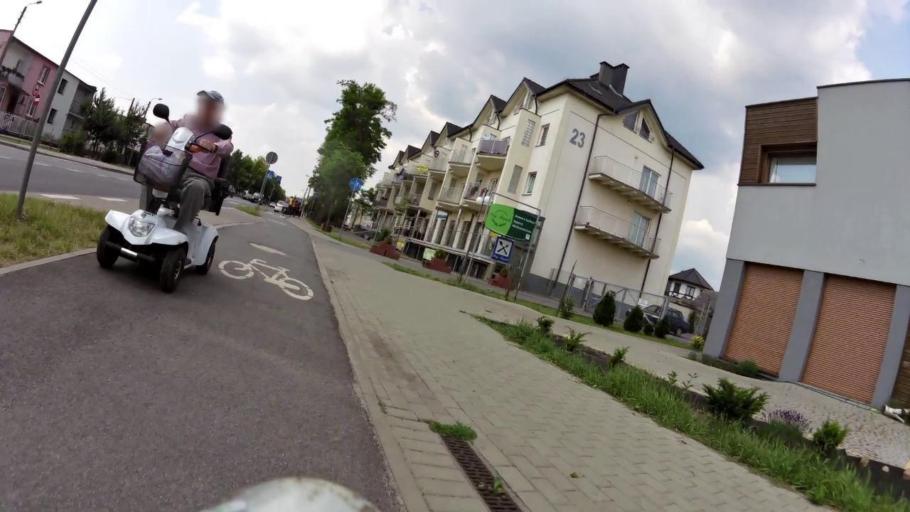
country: PL
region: Kujawsko-Pomorskie
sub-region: Powiat bydgoski
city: Koronowo
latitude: 53.3060
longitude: 17.9457
